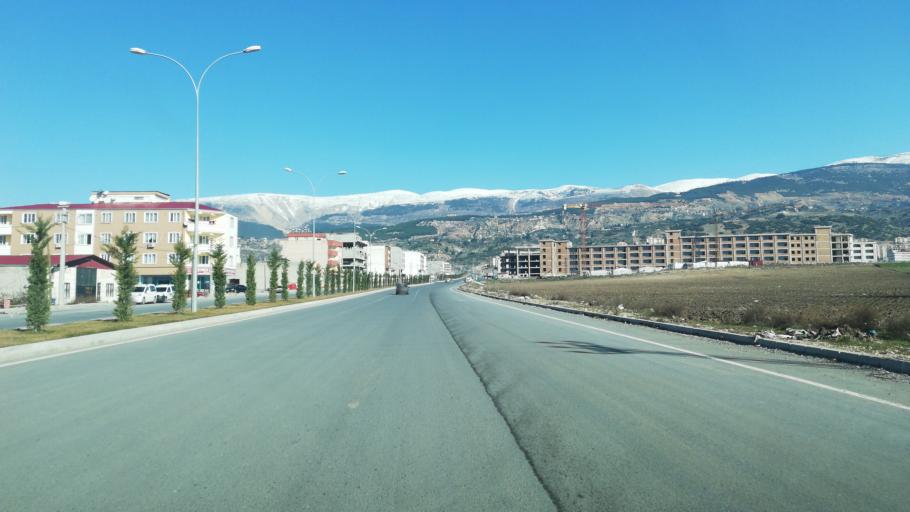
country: TR
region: Kahramanmaras
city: Kahramanmaras
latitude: 37.5720
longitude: 36.9747
